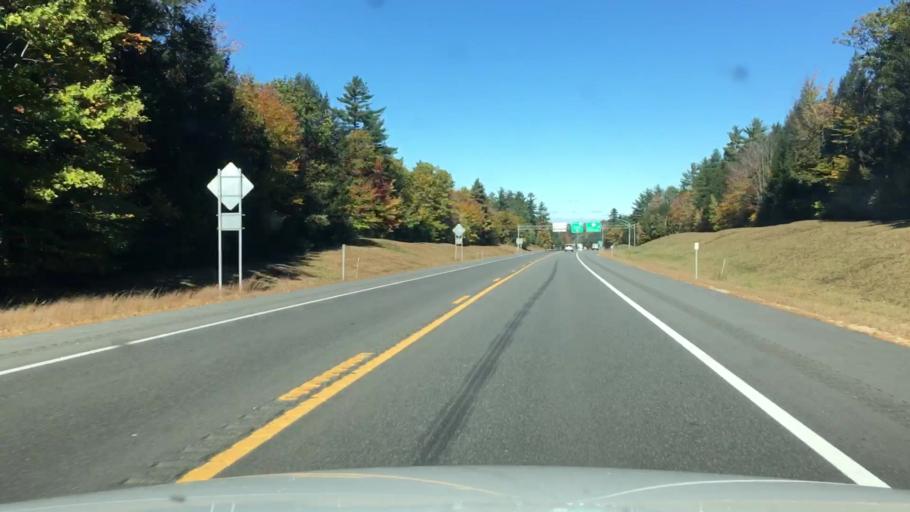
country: US
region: New Hampshire
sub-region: Carroll County
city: Sanbornville
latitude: 43.4734
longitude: -71.0018
